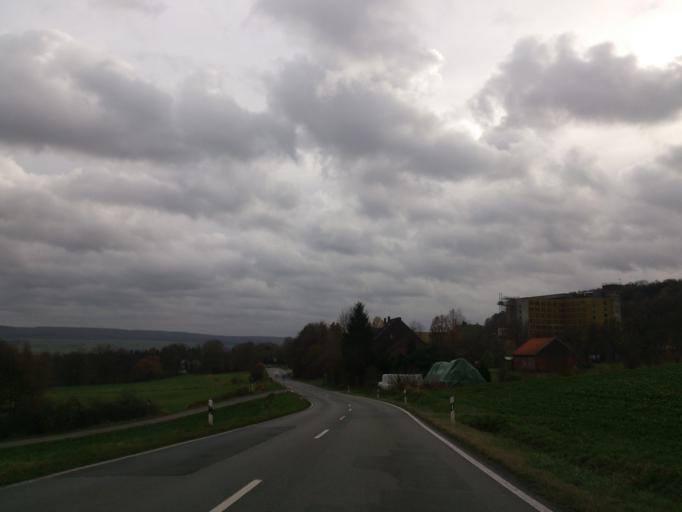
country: DE
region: North Rhine-Westphalia
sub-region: Regierungsbezirk Detmold
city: Hoexter
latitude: 51.7888
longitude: 9.3649
